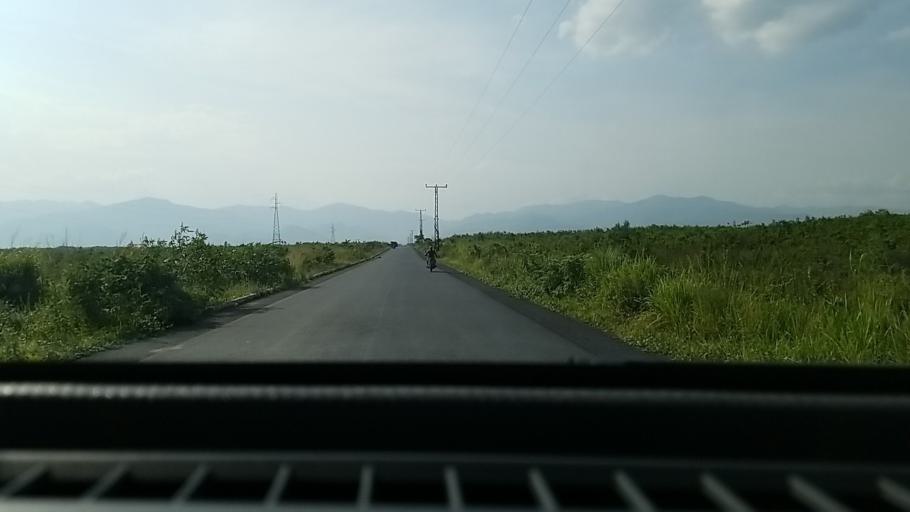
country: CD
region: Nord Kivu
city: Sake
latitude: -1.5982
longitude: 29.1103
